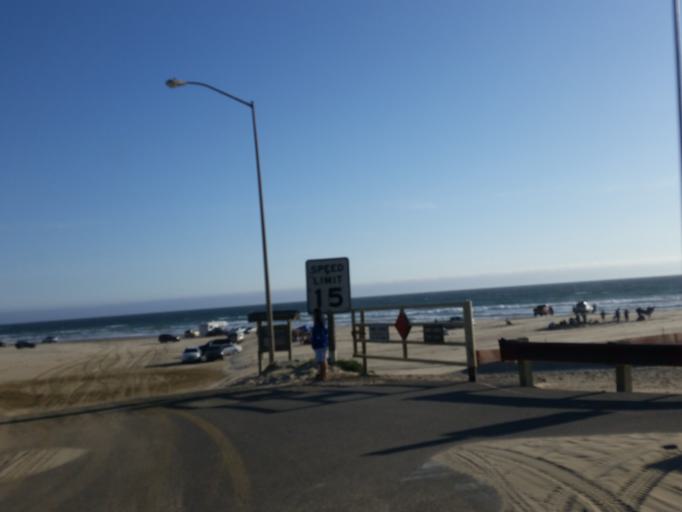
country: US
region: California
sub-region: San Luis Obispo County
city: Grover Beach
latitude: 35.1221
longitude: -120.6345
